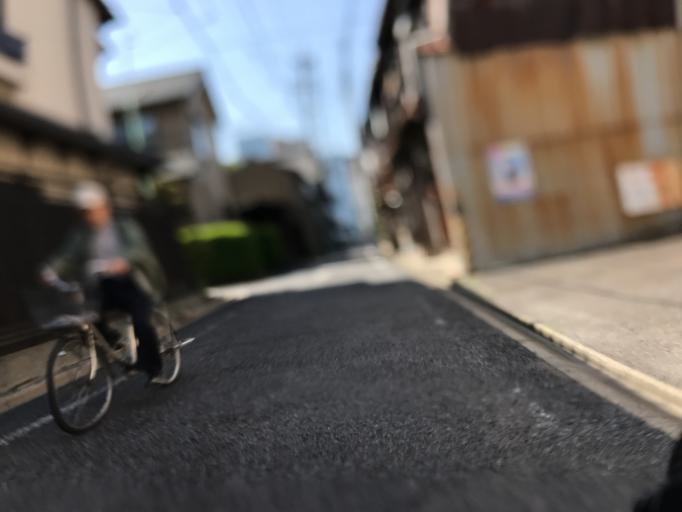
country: JP
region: Aichi
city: Nagoya-shi
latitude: 35.1753
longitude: 136.8918
